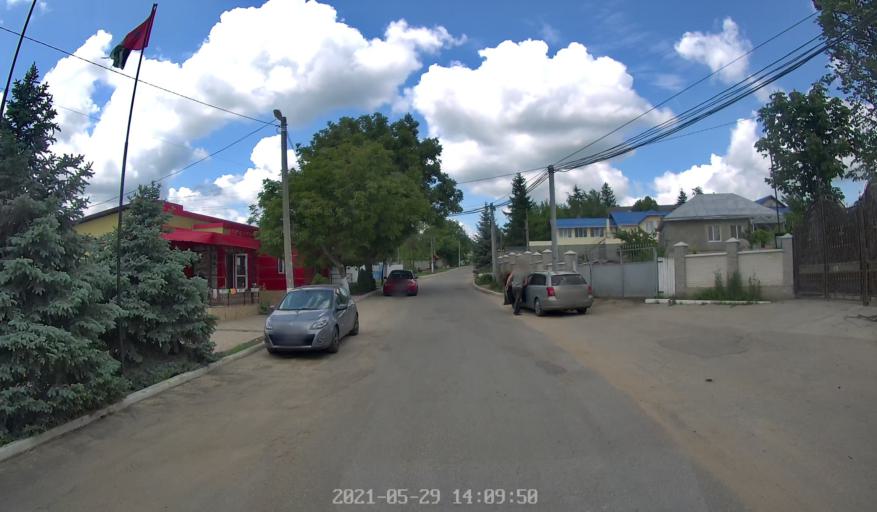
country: MD
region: Hincesti
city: Hincesti
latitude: 46.8248
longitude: 28.6733
